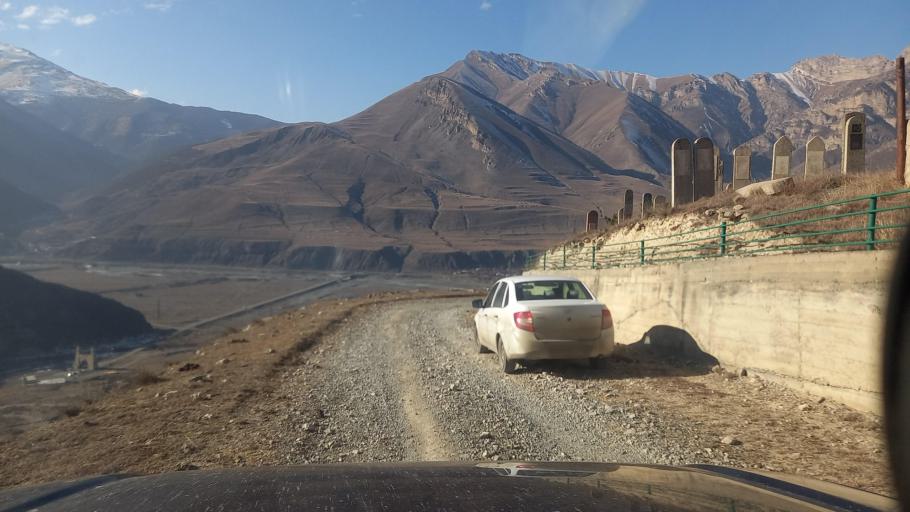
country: RU
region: Ingushetiya
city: Dzhayrakh
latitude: 42.8466
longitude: 44.6562
